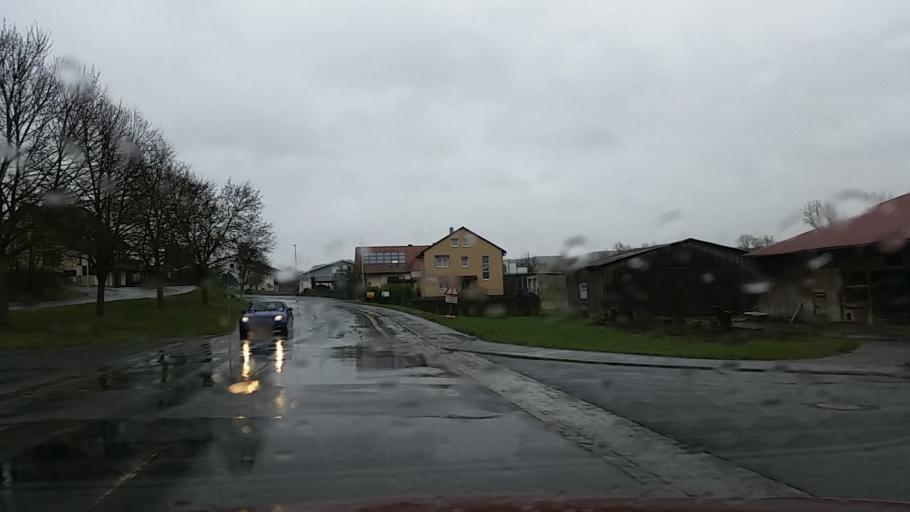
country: DE
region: Bavaria
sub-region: Regierungsbezirk Unterfranken
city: Birkenfeld
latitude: 49.8609
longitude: 9.7021
